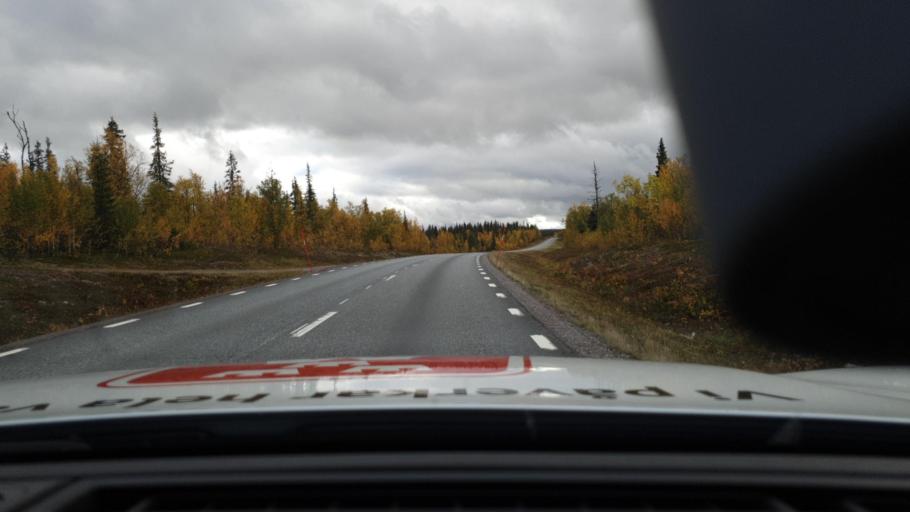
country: SE
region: Norrbotten
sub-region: Gallivare Kommun
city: Malmberget
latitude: 67.3231
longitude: 21.0828
